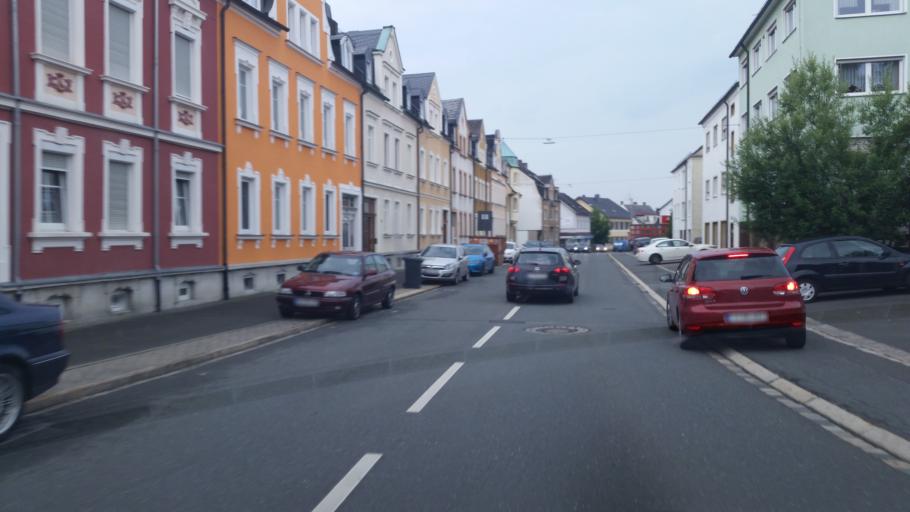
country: DE
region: Bavaria
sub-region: Upper Franconia
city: Rehau
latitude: 50.2463
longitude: 12.0407
